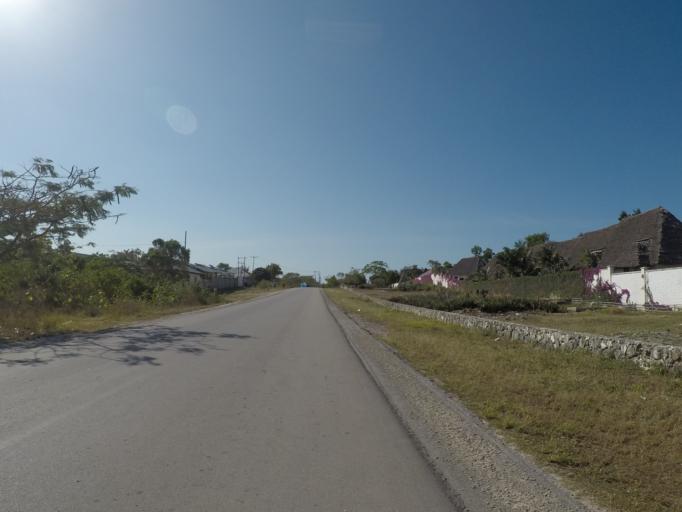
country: TZ
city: Kiwengwa
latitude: -6.1437
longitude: 39.5137
